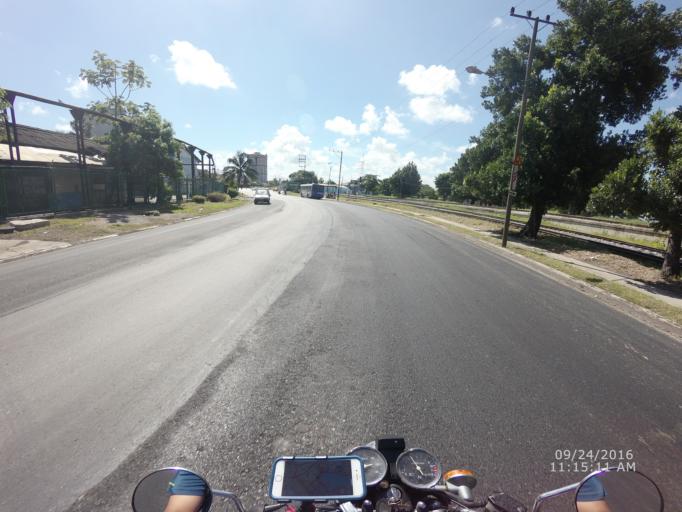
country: CU
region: La Habana
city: La Habana Vieja
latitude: 23.1196
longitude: -82.3591
